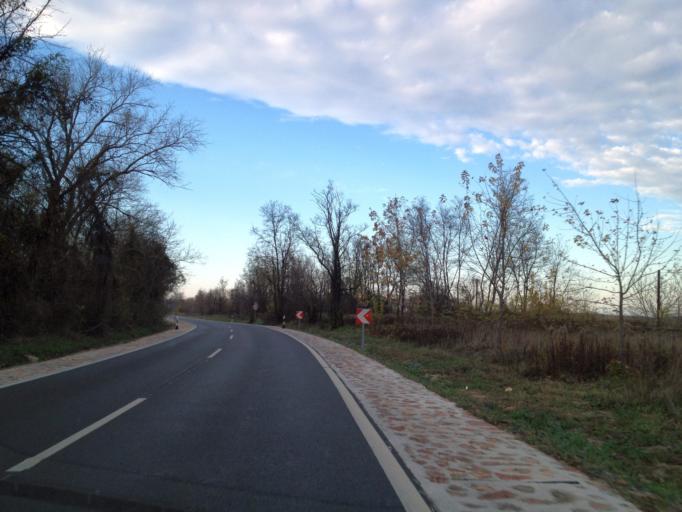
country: HU
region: Gyor-Moson-Sopron
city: Nyul
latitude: 47.6044
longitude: 17.6876
